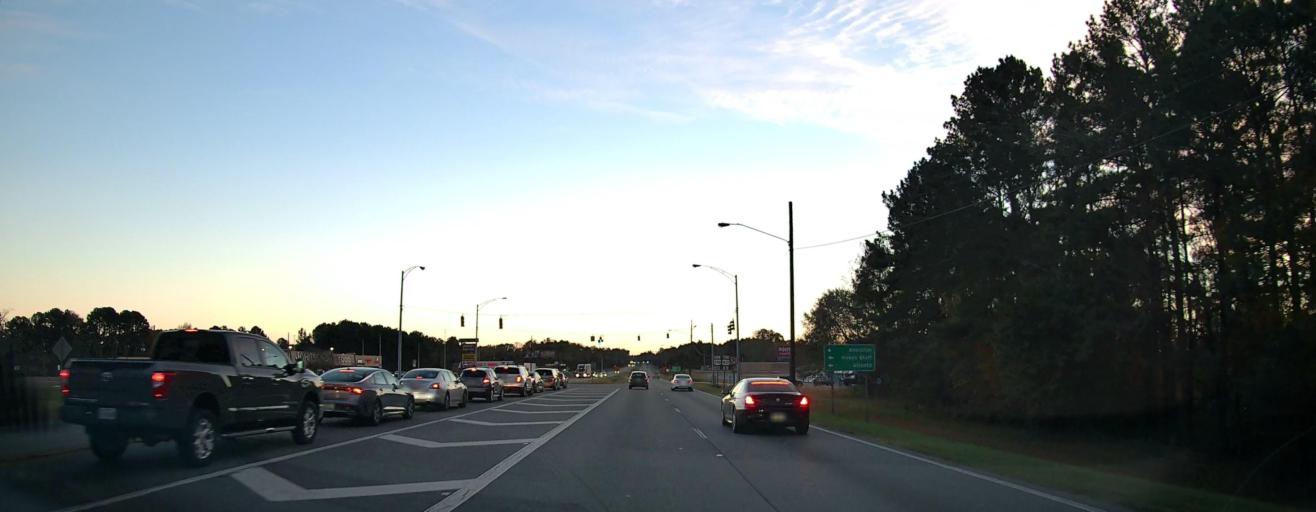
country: US
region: Alabama
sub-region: Etowah County
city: Gadsden
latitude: 33.9999
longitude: -85.9685
